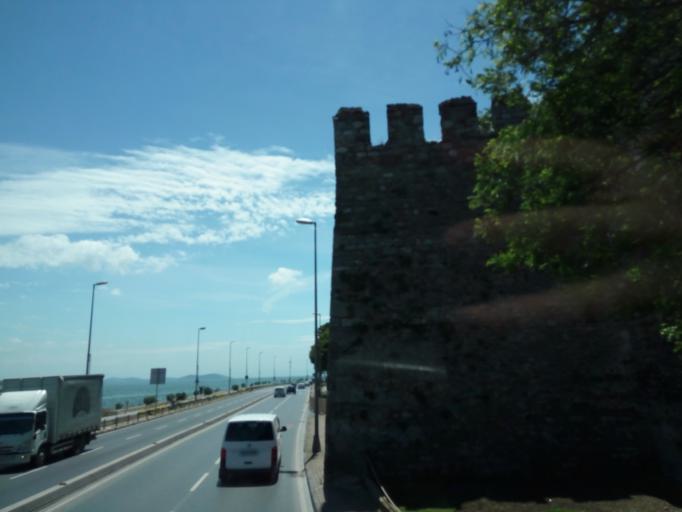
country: TR
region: Istanbul
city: Eminoenue
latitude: 41.0146
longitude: 28.9873
